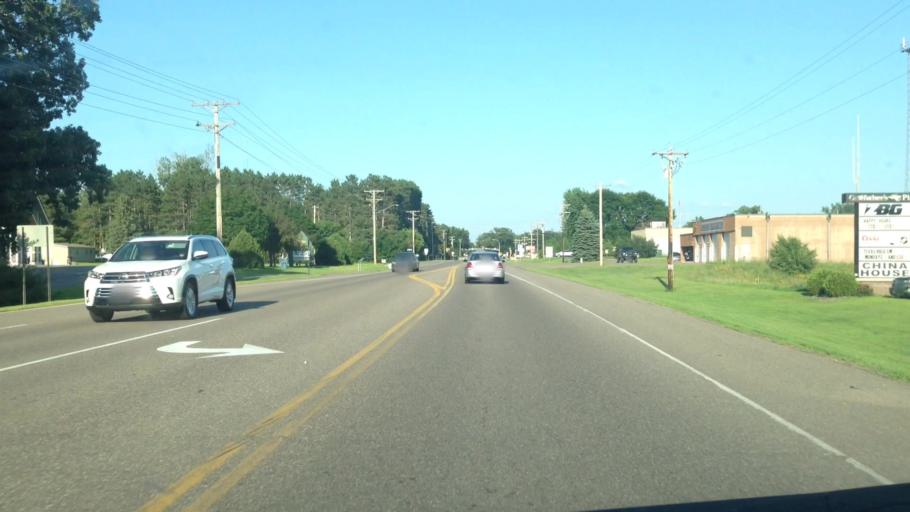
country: US
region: Minnesota
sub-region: Sherburne County
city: Zimmerman
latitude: 45.4434
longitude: -93.6013
